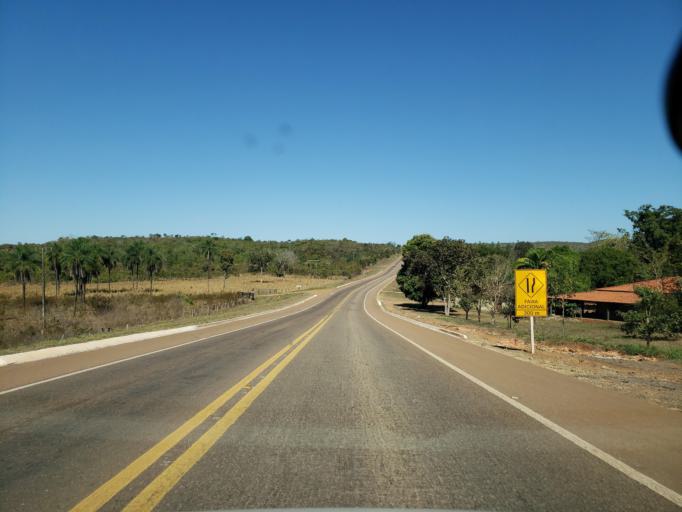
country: BR
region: Mato Grosso
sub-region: Poxoreo
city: Poxoreo
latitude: -15.7813
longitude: -54.3692
